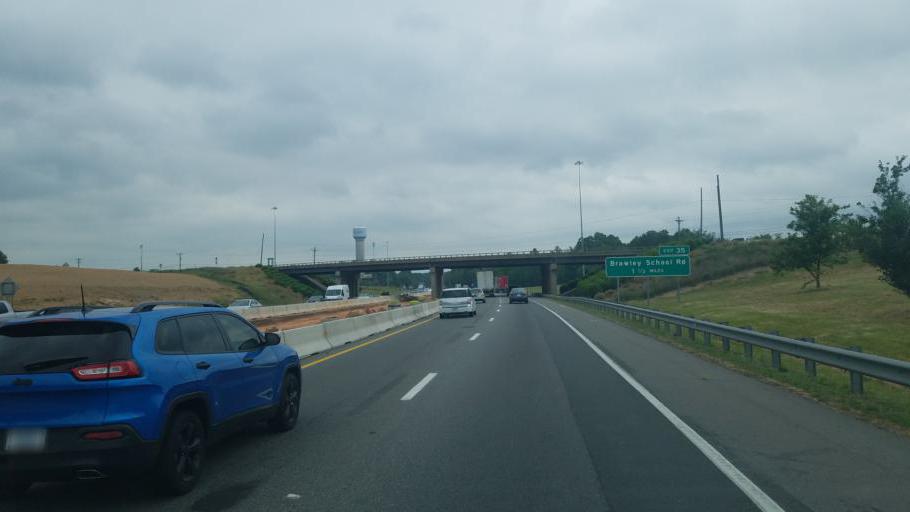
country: US
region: North Carolina
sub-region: Gaston County
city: Davidson
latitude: 35.5521
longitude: -80.8578
